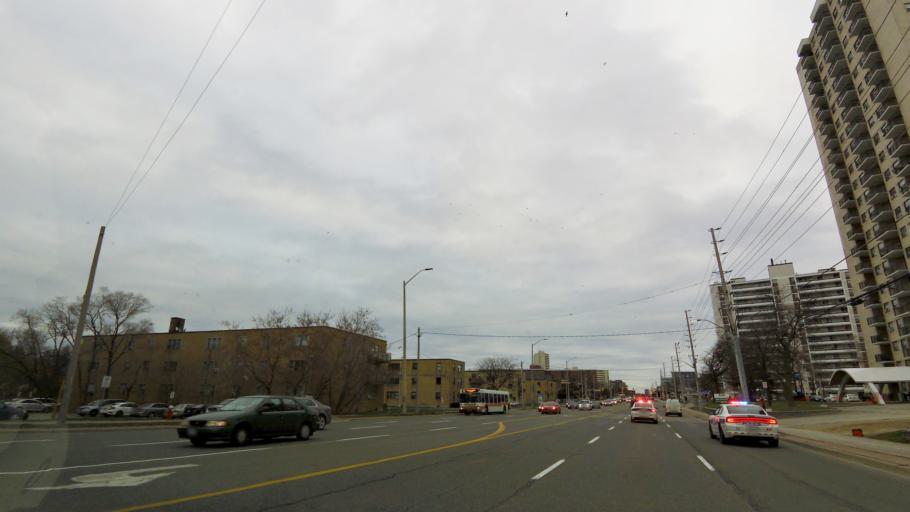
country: CA
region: Ontario
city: Mississauga
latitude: 43.5771
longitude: -79.6121
